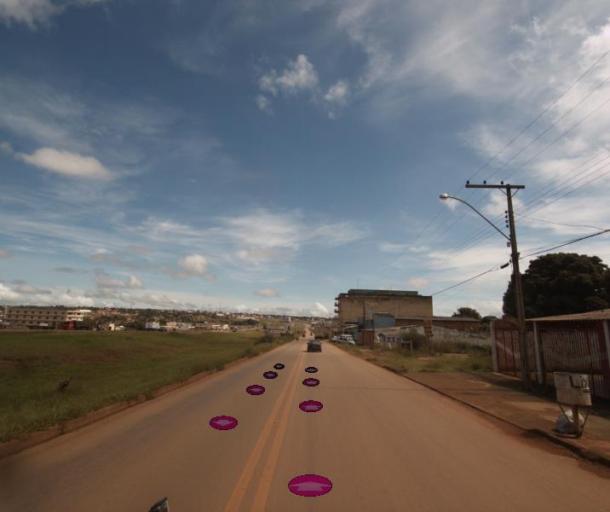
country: BR
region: Federal District
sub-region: Brasilia
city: Brasilia
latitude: -15.7434
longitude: -48.2675
